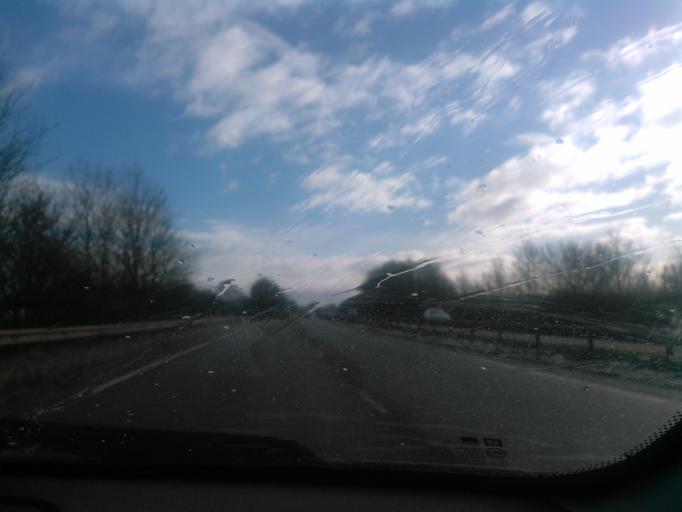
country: GB
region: England
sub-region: Staffordshire
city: Cheadle
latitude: 52.9507
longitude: -2.0174
